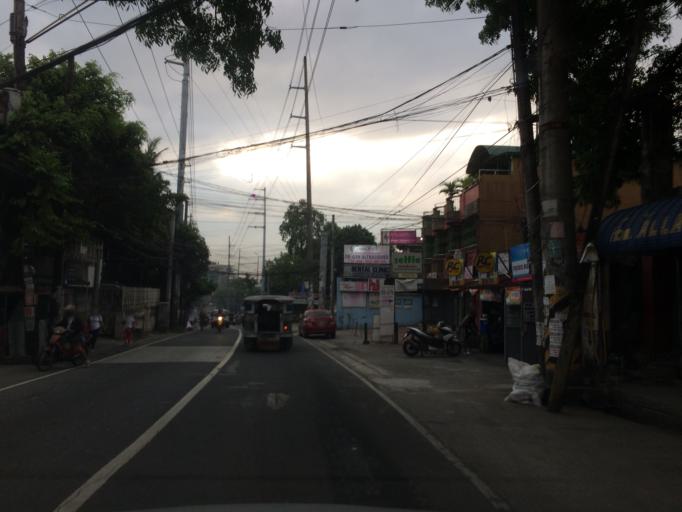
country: PH
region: Calabarzon
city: Bagong Pagasa
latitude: 14.6743
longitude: 121.0471
